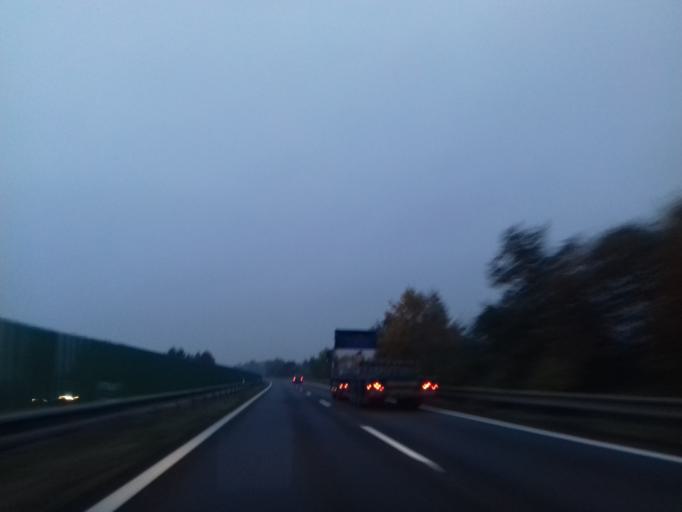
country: CZ
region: Olomoucky
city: Prikazy
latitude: 49.6429
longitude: 17.1362
